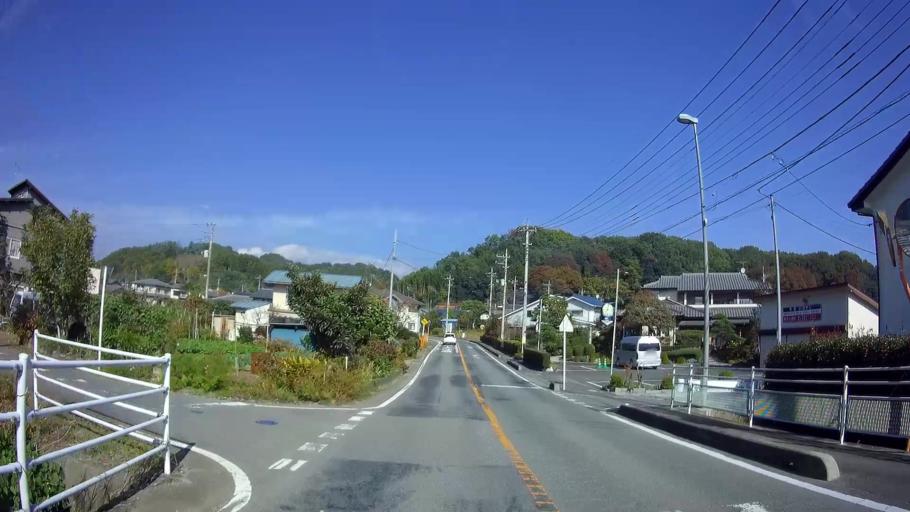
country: JP
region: Gunma
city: Annaka
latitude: 36.3379
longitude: 138.8926
